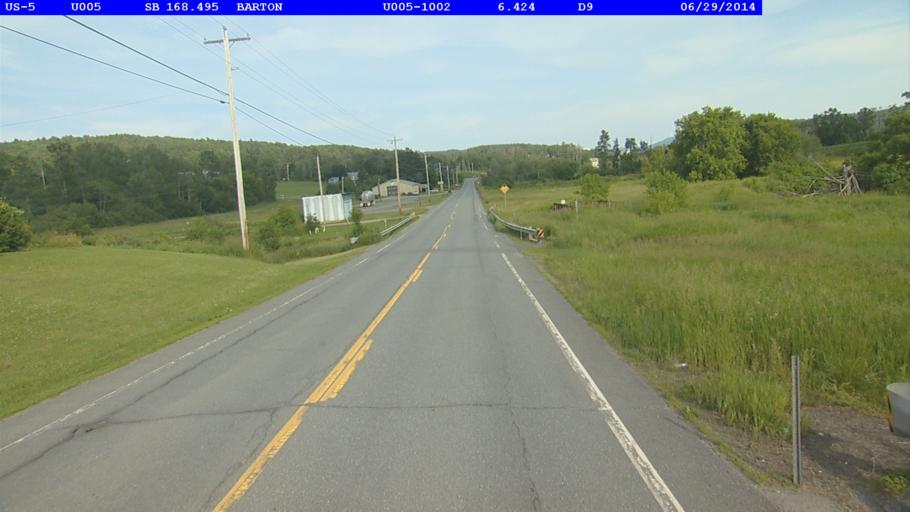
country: US
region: Vermont
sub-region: Orleans County
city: Newport
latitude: 44.7579
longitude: -72.1909
